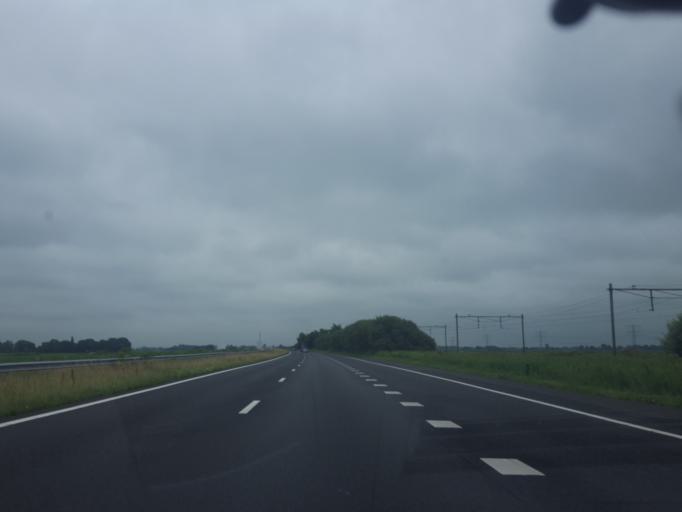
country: NL
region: Friesland
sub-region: Gemeente Leeuwarden
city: Wirdum
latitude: 53.1421
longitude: 5.7973
